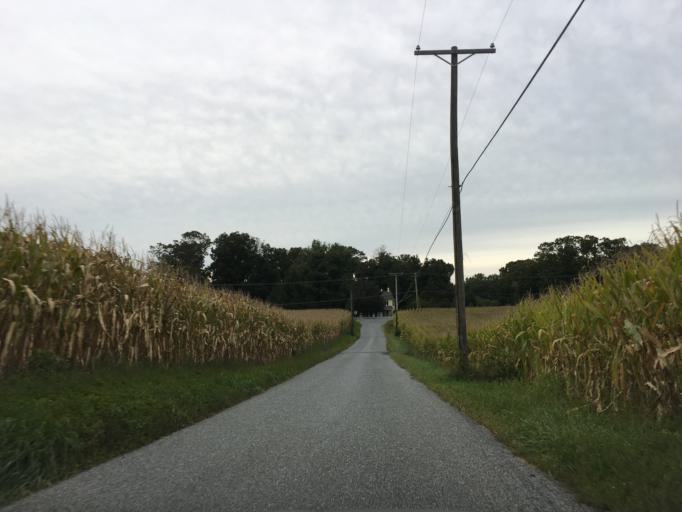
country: US
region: Maryland
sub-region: Baltimore County
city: Hunt Valley
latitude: 39.5888
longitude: -76.6876
